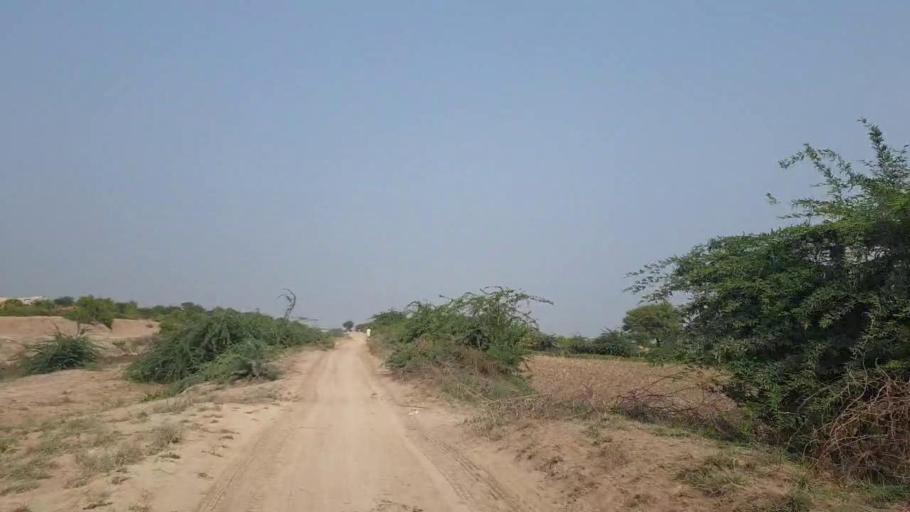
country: PK
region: Sindh
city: Badin
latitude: 24.7019
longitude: 68.7766
